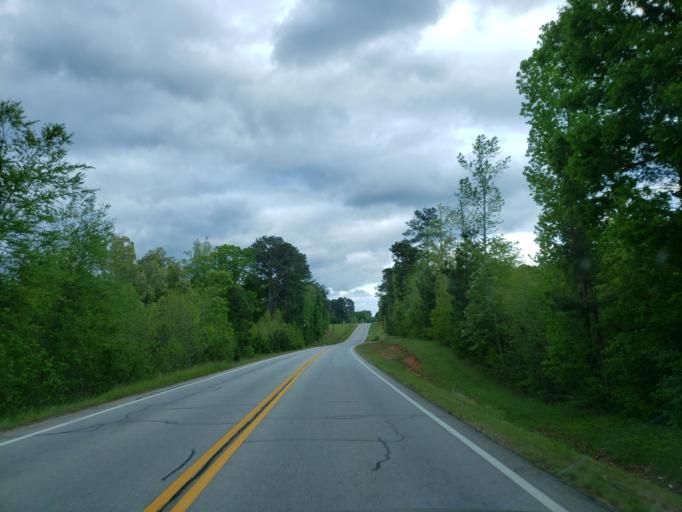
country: US
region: Georgia
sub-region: Haralson County
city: Buchanan
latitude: 33.8163
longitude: -85.1200
